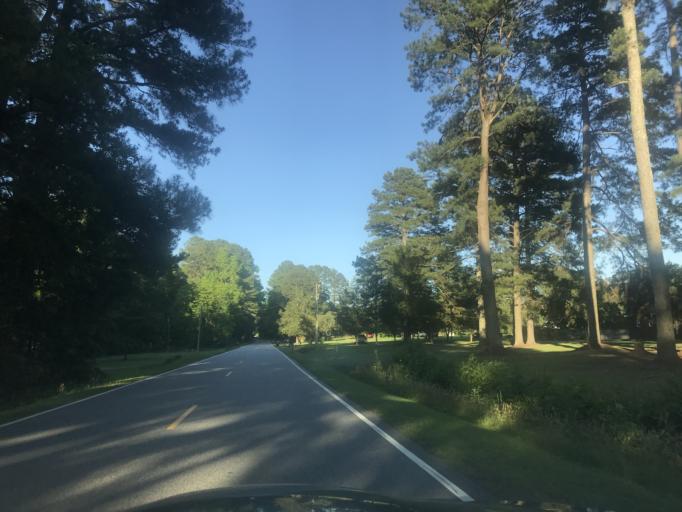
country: US
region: North Carolina
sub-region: Johnston County
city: Archer Lodge
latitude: 35.7307
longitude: -78.4094
